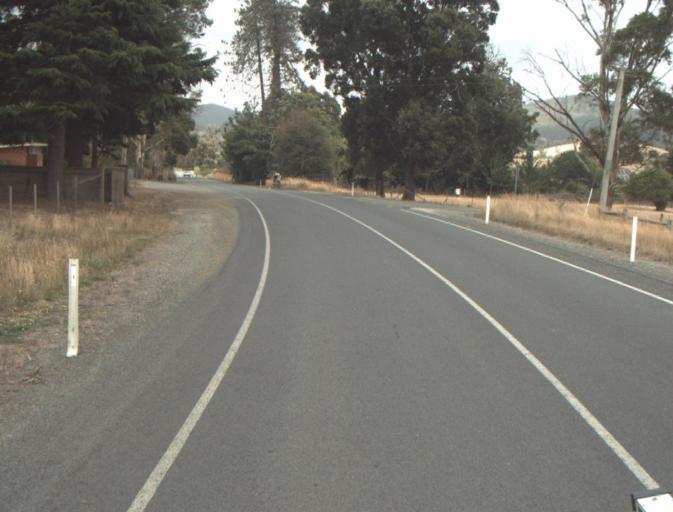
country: AU
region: Tasmania
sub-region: Launceston
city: Mayfield
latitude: -41.2290
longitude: 147.2090
